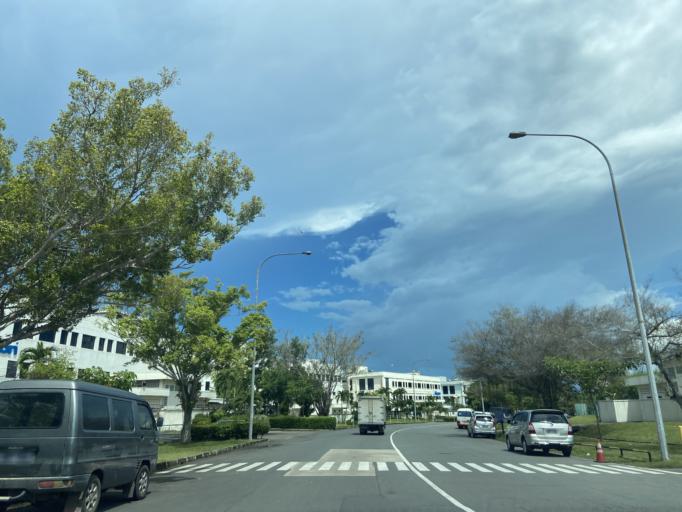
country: SG
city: Singapore
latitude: 1.0638
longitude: 104.0334
